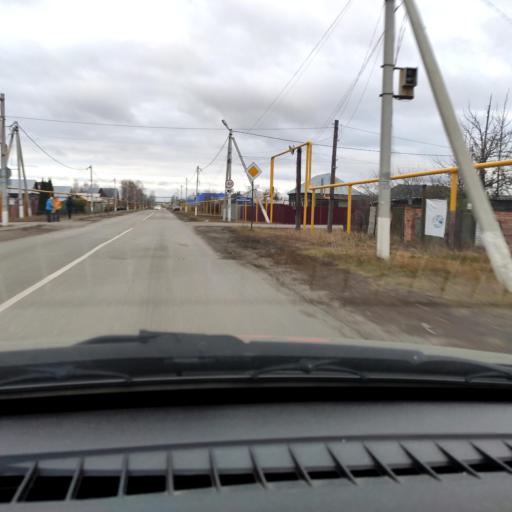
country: RU
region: Samara
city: Podstepki
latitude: 53.5161
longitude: 49.1253
